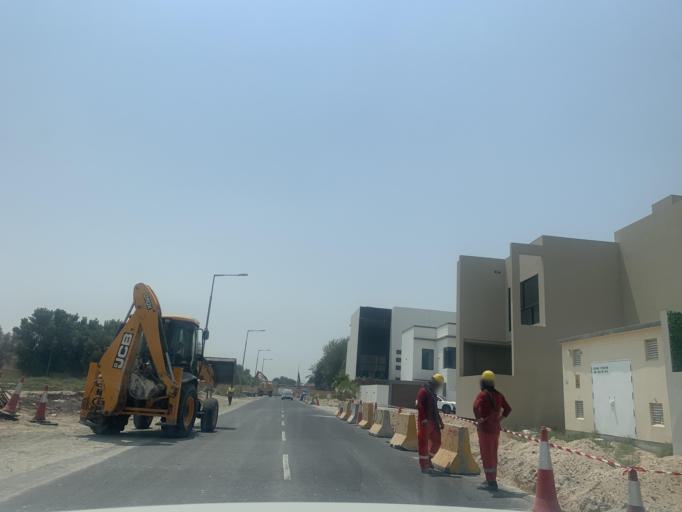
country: BH
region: Central Governorate
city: Madinat Hamad
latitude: 26.1471
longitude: 50.4666
